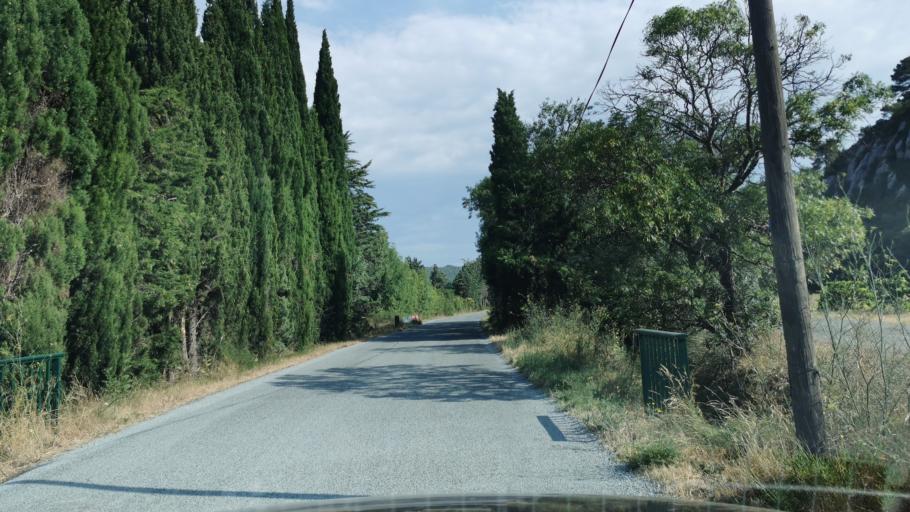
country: FR
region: Languedoc-Roussillon
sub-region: Departement de l'Aude
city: Bize-Minervois
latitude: 43.3338
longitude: 2.8766
